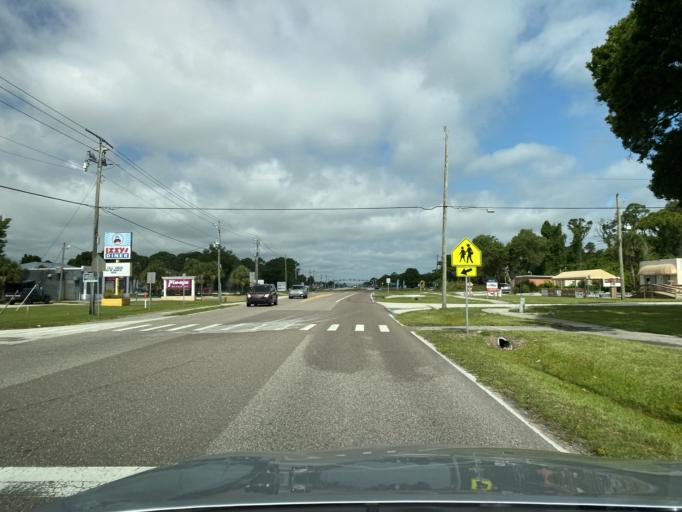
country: US
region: Florida
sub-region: Brevard County
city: Palm Bay
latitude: 28.0346
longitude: -80.5929
